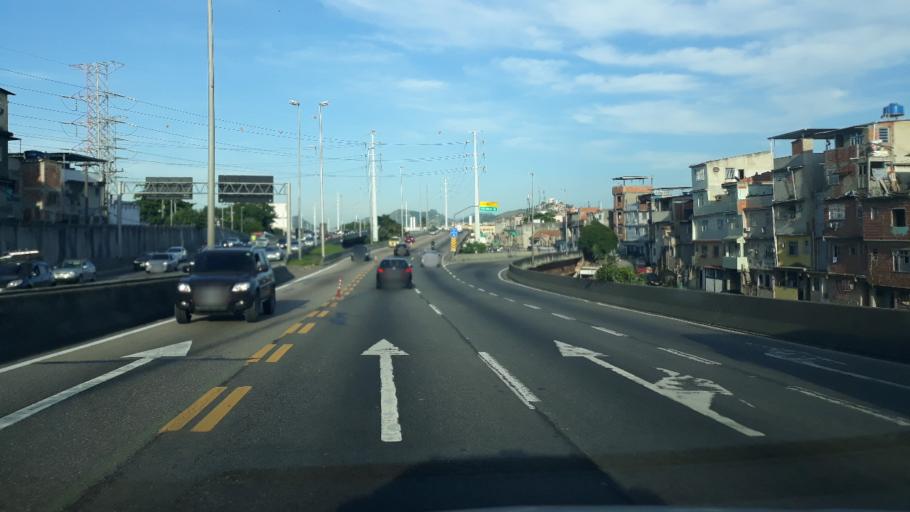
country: BR
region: Rio de Janeiro
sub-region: Rio De Janeiro
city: Rio de Janeiro
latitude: -22.8717
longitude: -43.2556
